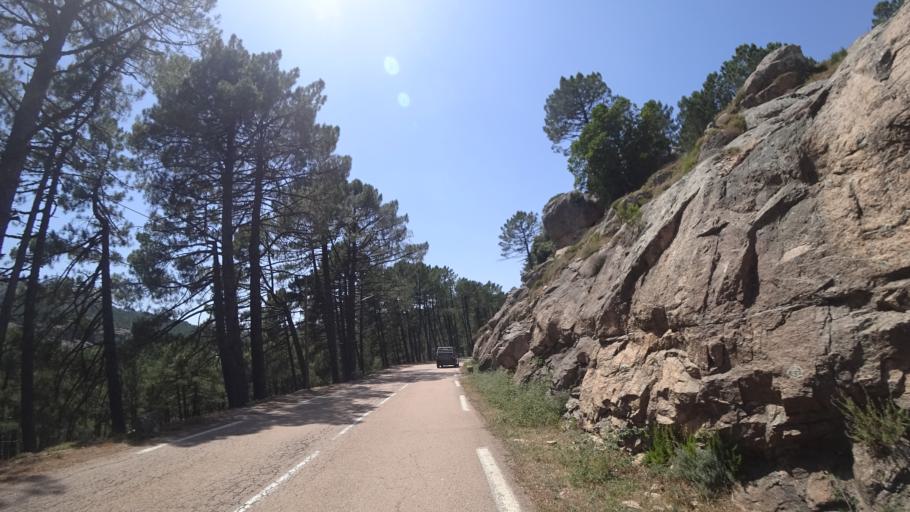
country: FR
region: Corsica
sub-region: Departement de la Corse-du-Sud
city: Zonza
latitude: 41.6710
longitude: 9.2080
